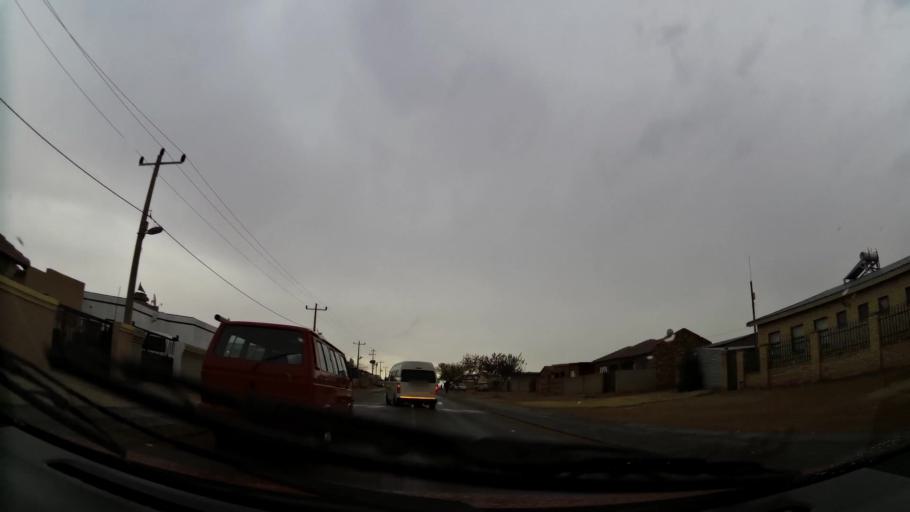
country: ZA
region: Gauteng
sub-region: City of Johannesburg Metropolitan Municipality
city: Roodepoort
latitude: -26.1769
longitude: 27.7908
